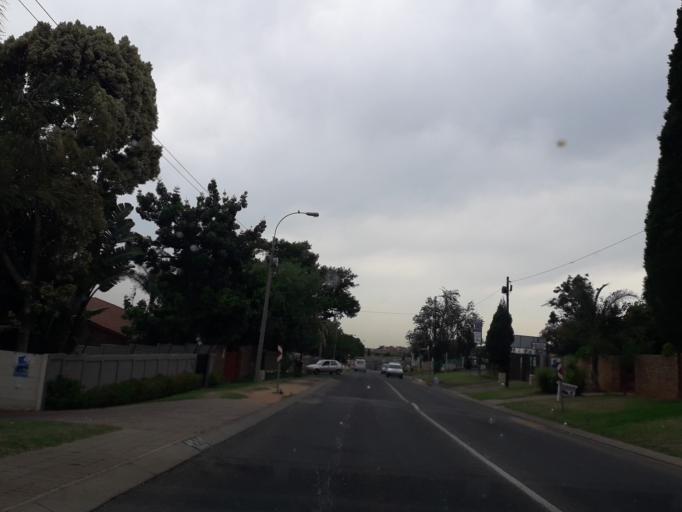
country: ZA
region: Gauteng
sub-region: City of Johannesburg Metropolitan Municipality
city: Roodepoort
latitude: -26.1054
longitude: 27.9226
